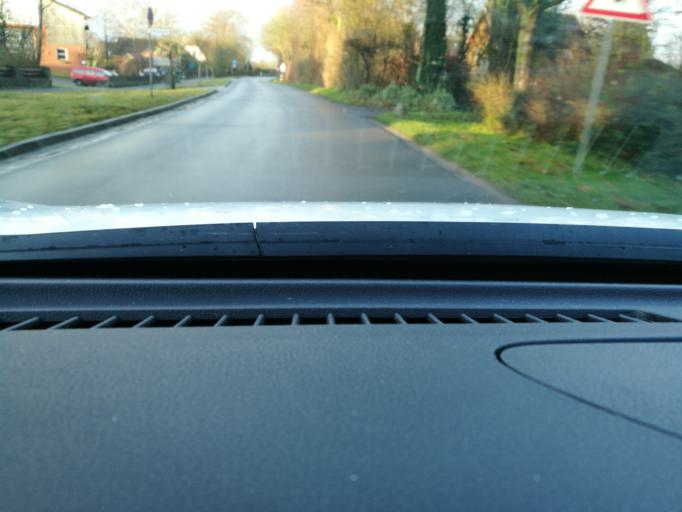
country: DE
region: Schleswig-Holstein
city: Holzbunge
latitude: 54.3984
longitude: 9.7020
